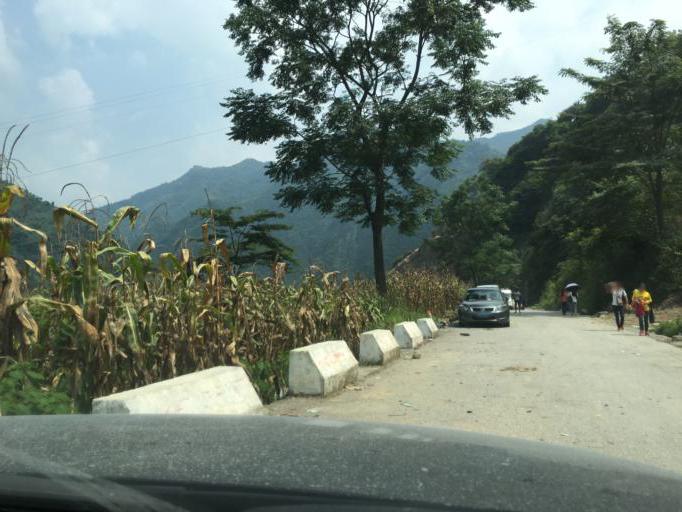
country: CN
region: Guangxi Zhuangzu Zizhiqu
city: Tongle
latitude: 25.3000
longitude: 106.2697
